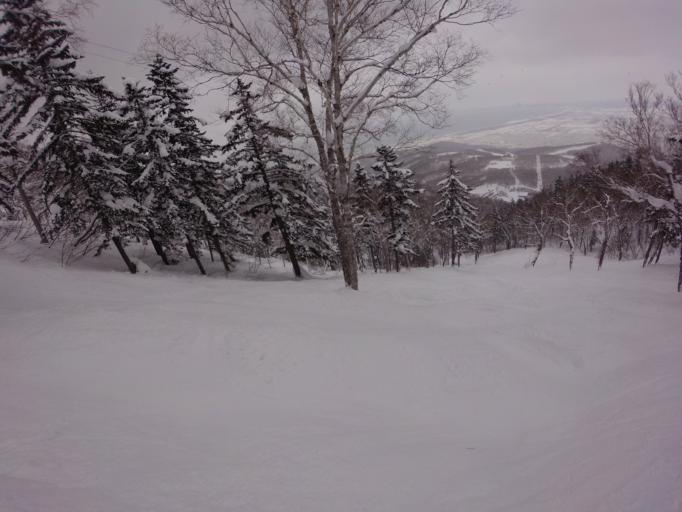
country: JP
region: Hokkaido
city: Sapporo
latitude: 43.0782
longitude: 141.1985
